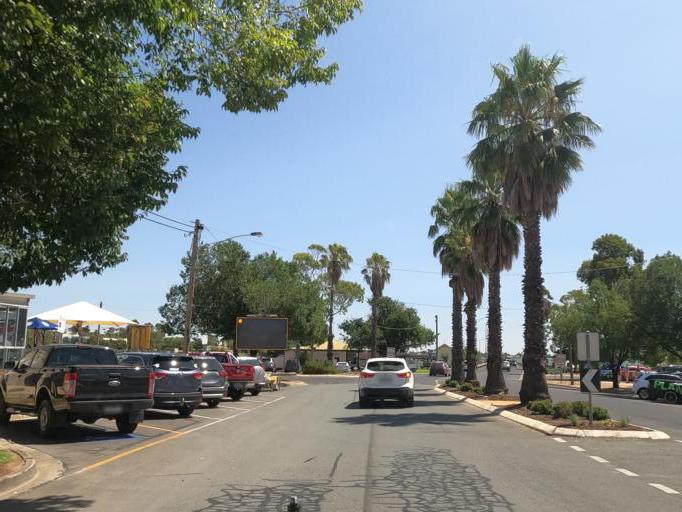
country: AU
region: Victoria
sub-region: Moira
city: Yarrawonga
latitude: -36.0089
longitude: 146.0044
